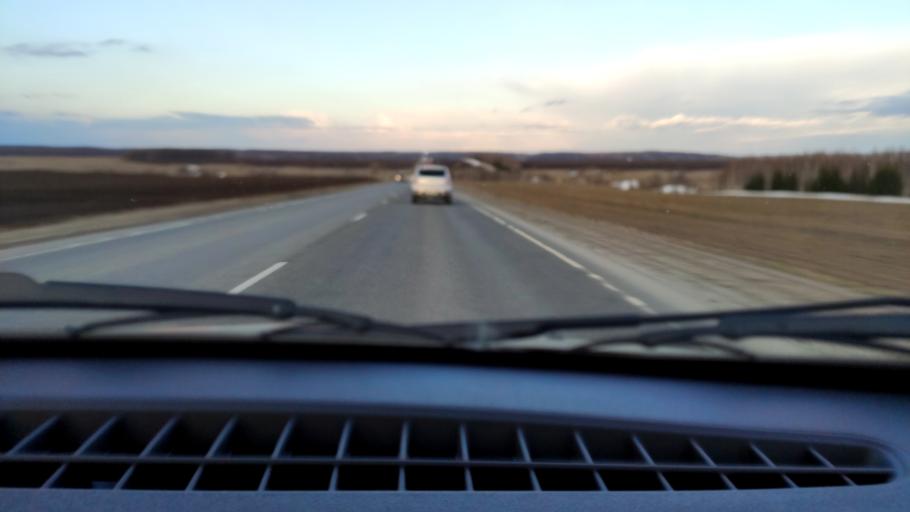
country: RU
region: Bashkortostan
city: Iglino
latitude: 54.7541
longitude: 56.3521
